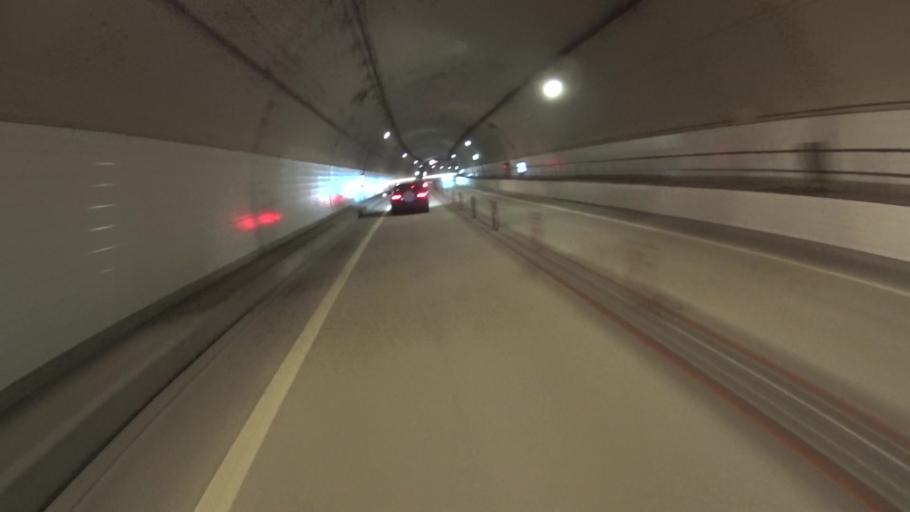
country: JP
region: Kyoto
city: Miyazu
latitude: 35.5388
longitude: 135.1596
